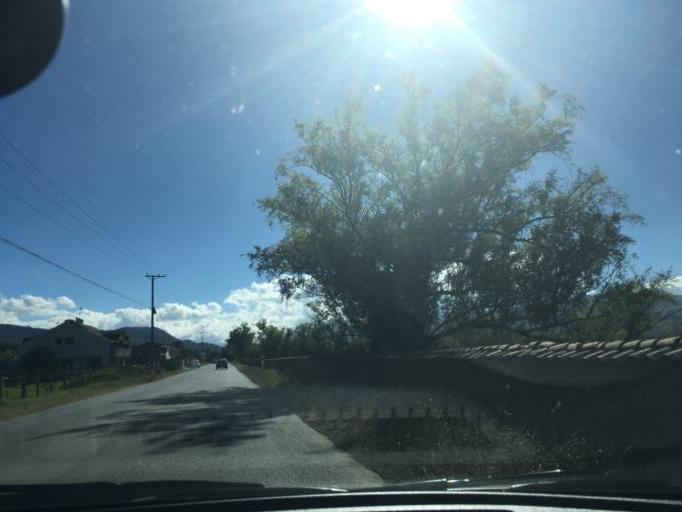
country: CO
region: Boyaca
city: Firavitoba
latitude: 5.6530
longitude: -72.9835
